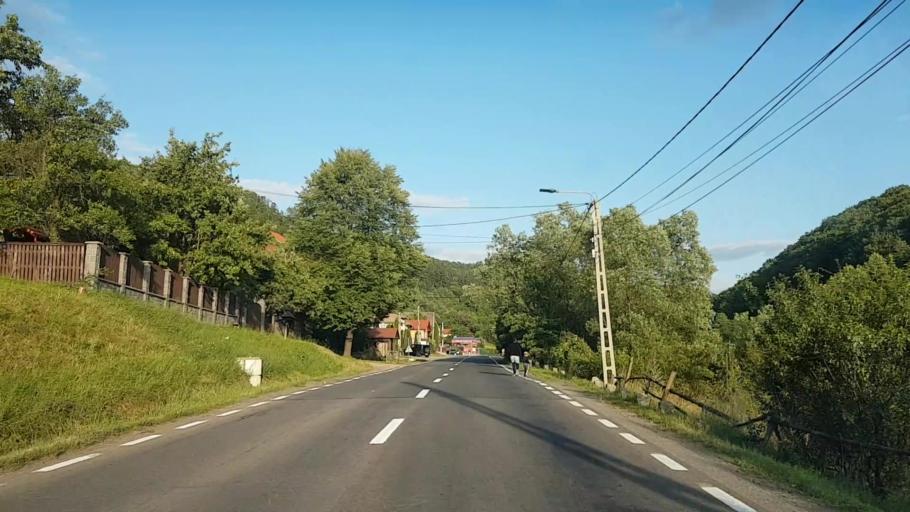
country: RO
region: Harghita
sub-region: Comuna Corund
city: Corund
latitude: 46.4688
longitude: 25.1993
